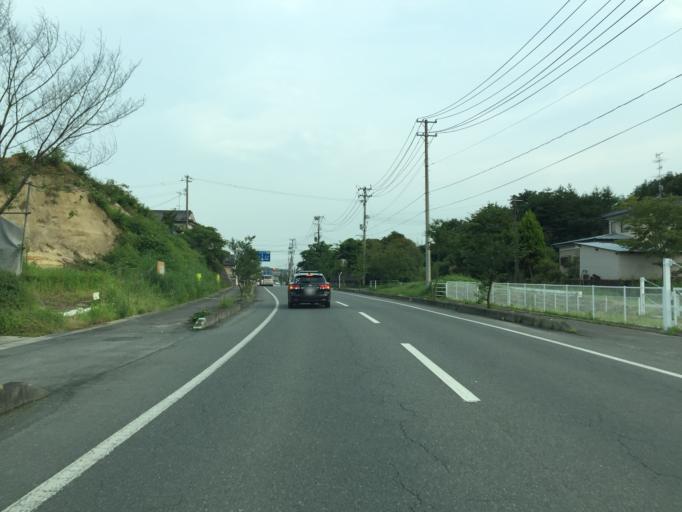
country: JP
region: Miyagi
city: Marumori
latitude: 37.7940
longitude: 140.9106
